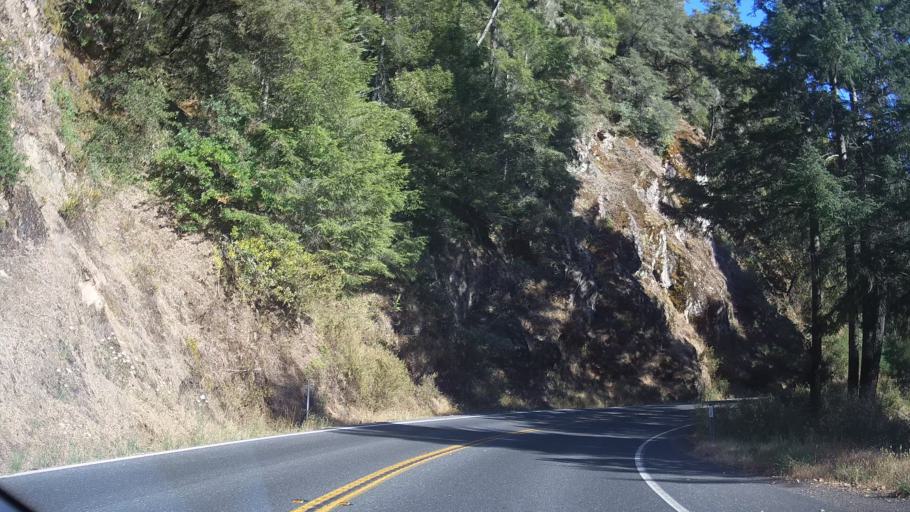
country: US
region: California
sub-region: Mendocino County
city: Brooktrails
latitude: 39.3746
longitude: -123.4952
